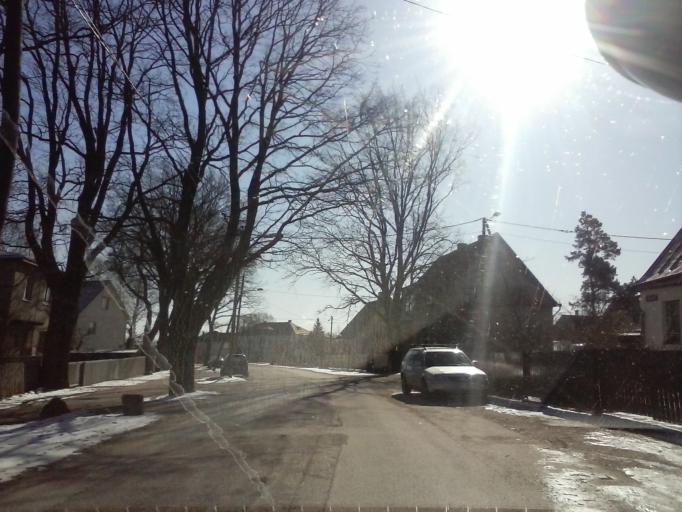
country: EE
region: Tartu
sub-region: Tartu linn
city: Tartu
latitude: 58.3640
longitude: 26.7123
